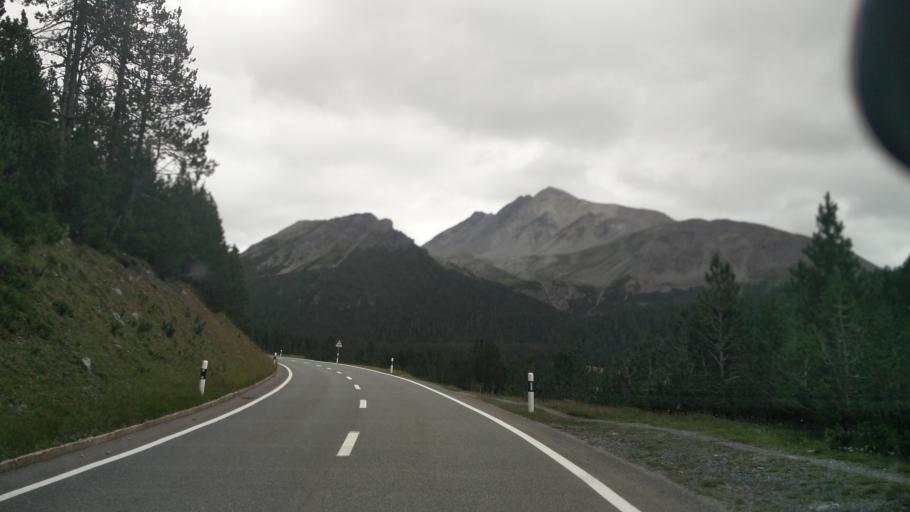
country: CH
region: Grisons
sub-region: Inn District
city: Scuol
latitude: 46.6493
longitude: 10.2645
